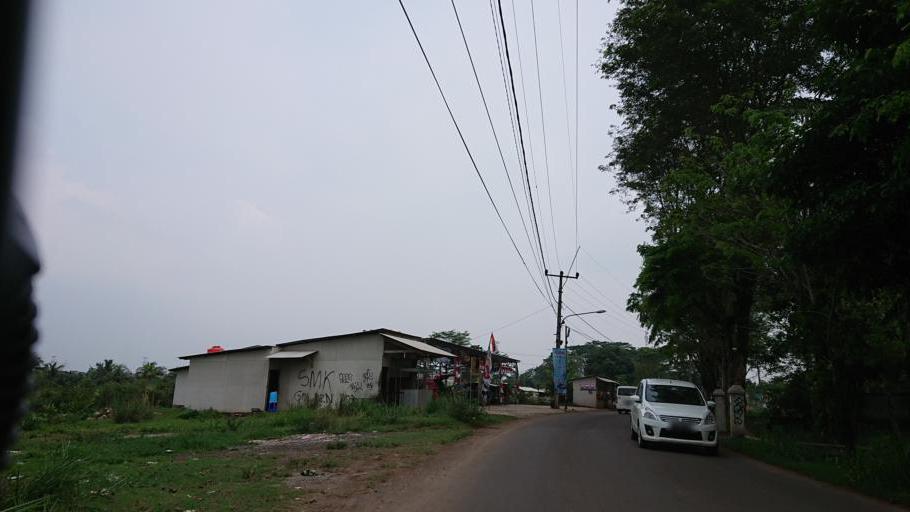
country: ID
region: West Java
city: Parung
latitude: -6.4560
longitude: 106.7054
